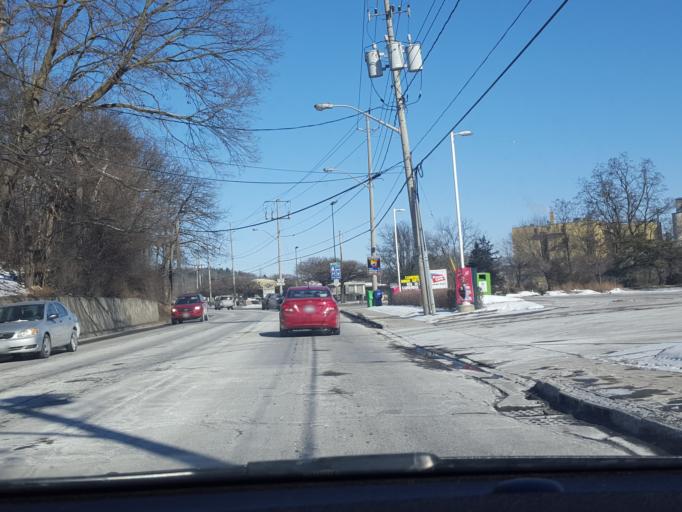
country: CA
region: Ontario
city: Cambridge
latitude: 43.3979
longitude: -80.3710
